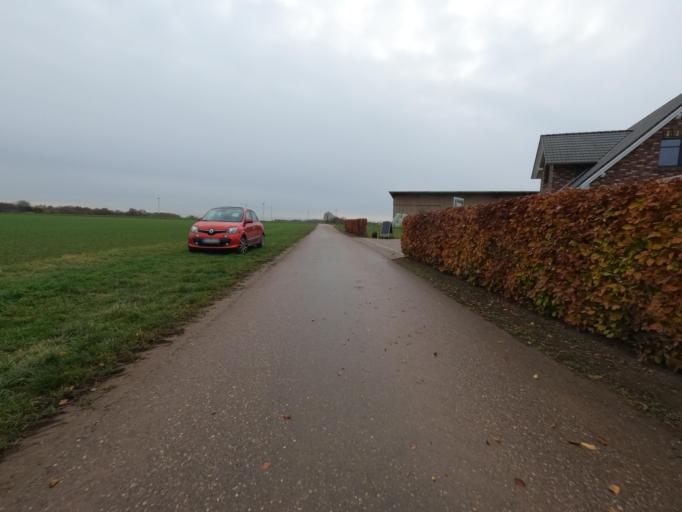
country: DE
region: North Rhine-Westphalia
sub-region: Regierungsbezirk Koln
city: Heinsberg
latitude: 51.0397
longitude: 6.1356
